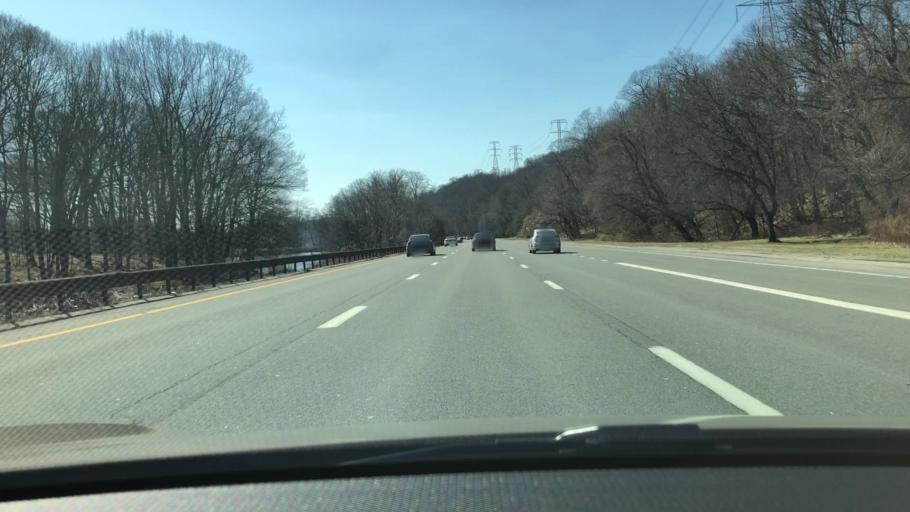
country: US
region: New York
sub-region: Westchester County
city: Greenville
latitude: 40.9871
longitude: -73.8420
